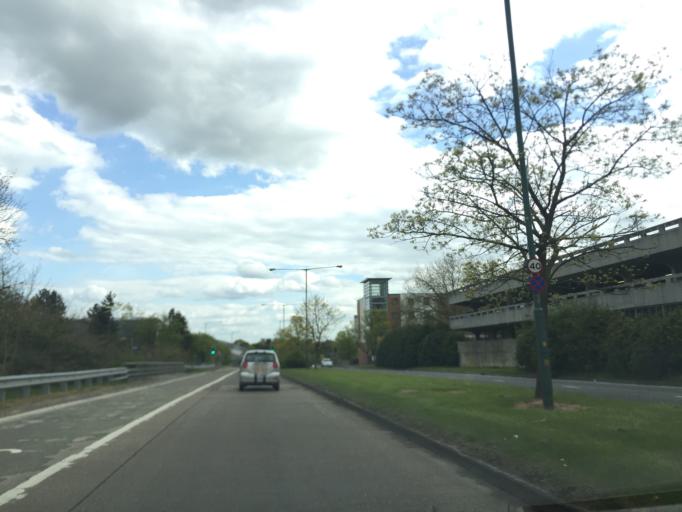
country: GB
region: England
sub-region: Essex
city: Harlow
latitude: 51.7705
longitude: 0.0968
